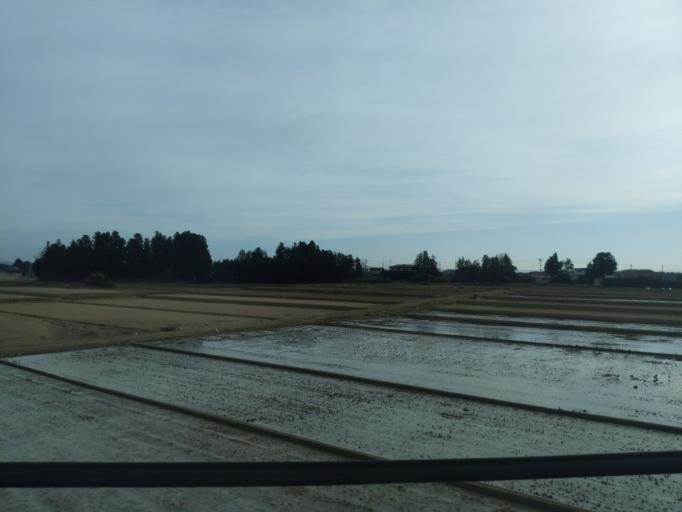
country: JP
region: Iwate
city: Ichinoseki
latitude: 38.7673
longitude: 141.0822
